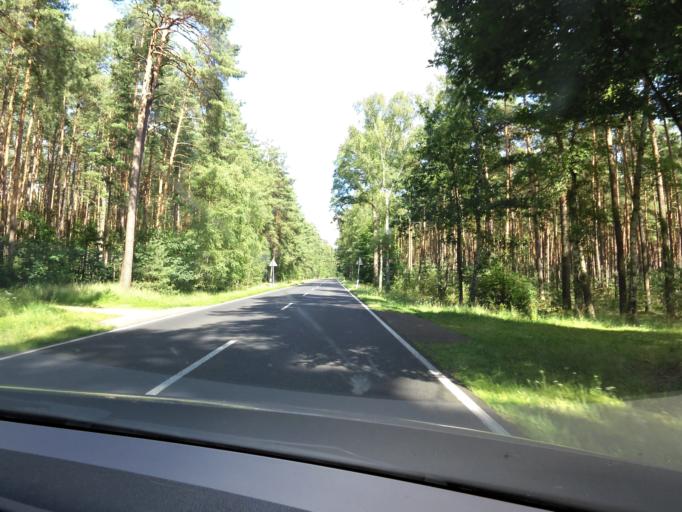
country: DE
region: Brandenburg
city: Furstenberg
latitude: 53.1975
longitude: 13.1880
